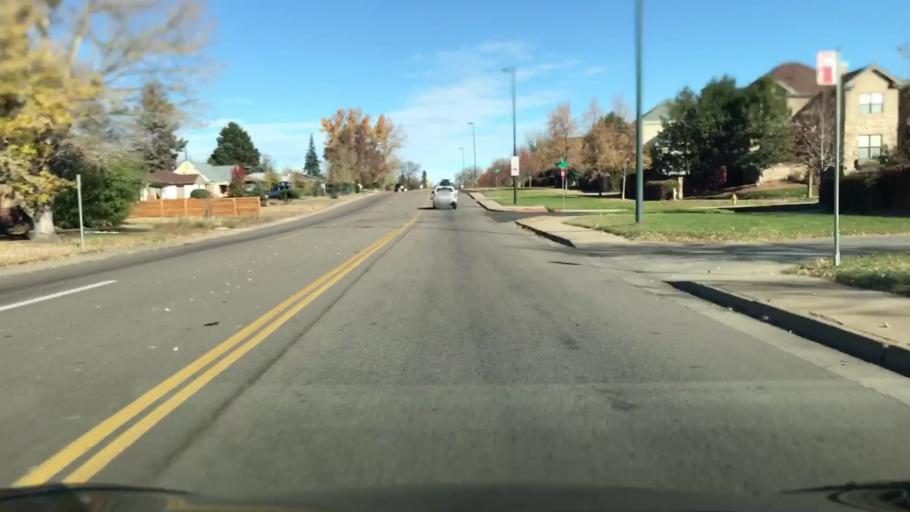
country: US
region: Colorado
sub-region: Arapahoe County
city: Glendale
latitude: 39.7297
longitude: -104.9035
